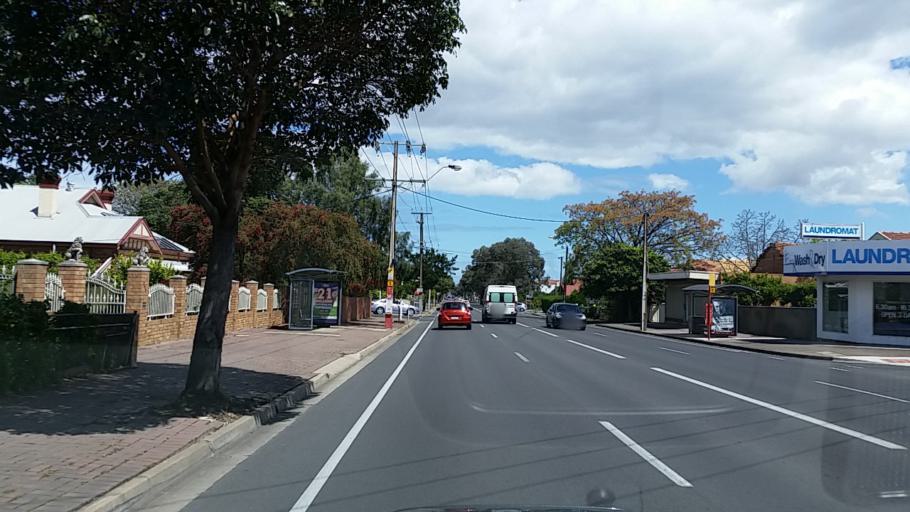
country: AU
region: South Australia
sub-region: Norwood Payneham St Peters
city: Trinity Gardens
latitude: -34.9144
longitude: 138.6502
